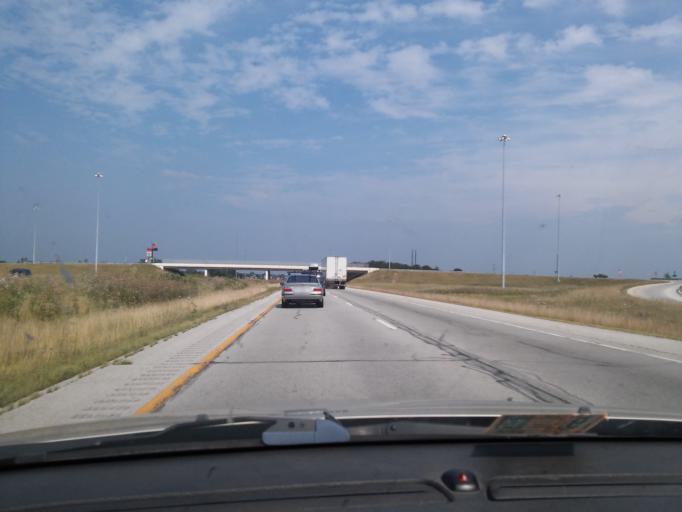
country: US
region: Ohio
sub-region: Preble County
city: Eaton
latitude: 39.8353
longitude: -84.6326
